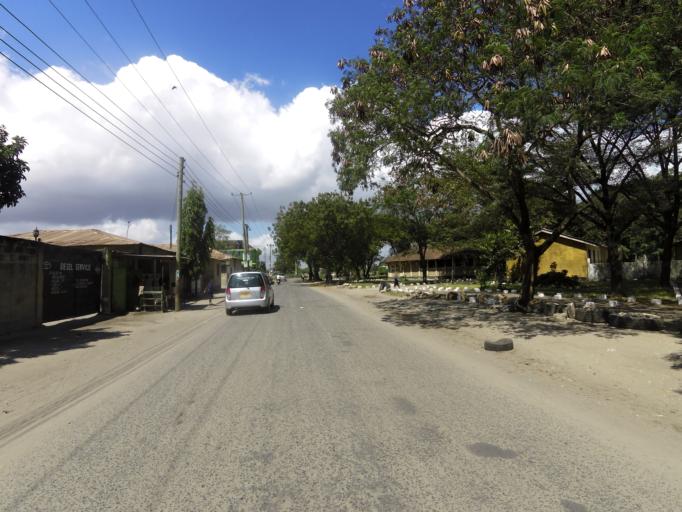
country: TZ
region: Dar es Salaam
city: Magomeni
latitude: -6.8031
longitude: 39.2576
